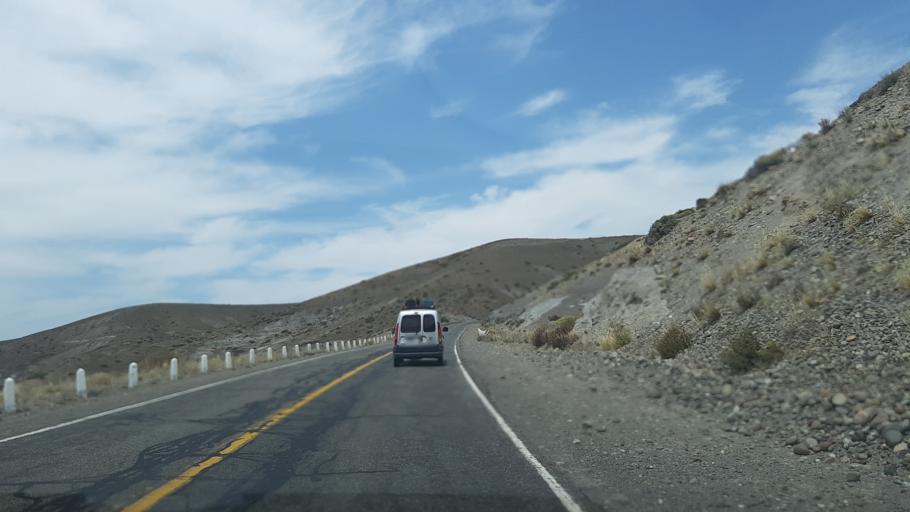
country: AR
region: Rio Negro
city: Pilcaniyeu
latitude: -40.4658
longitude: -70.6578
